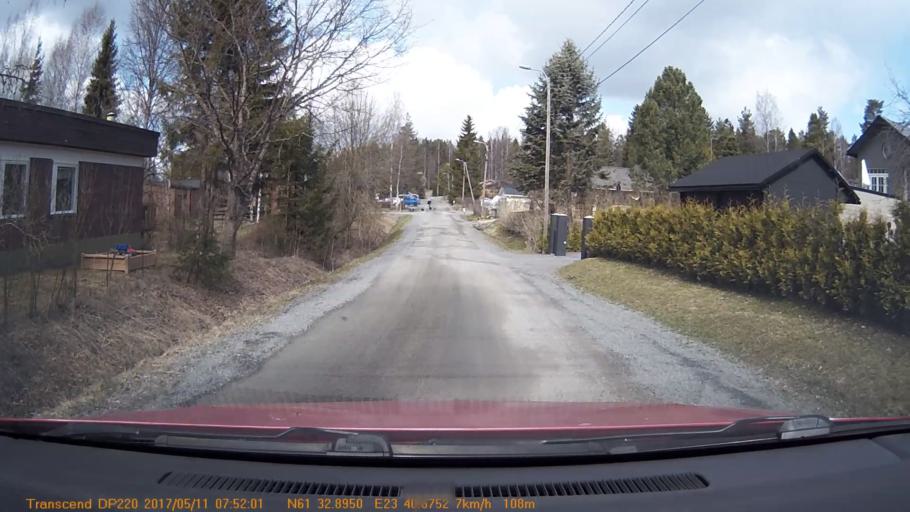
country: FI
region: Pirkanmaa
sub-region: Tampere
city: Yloejaervi
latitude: 61.5483
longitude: 23.6778
